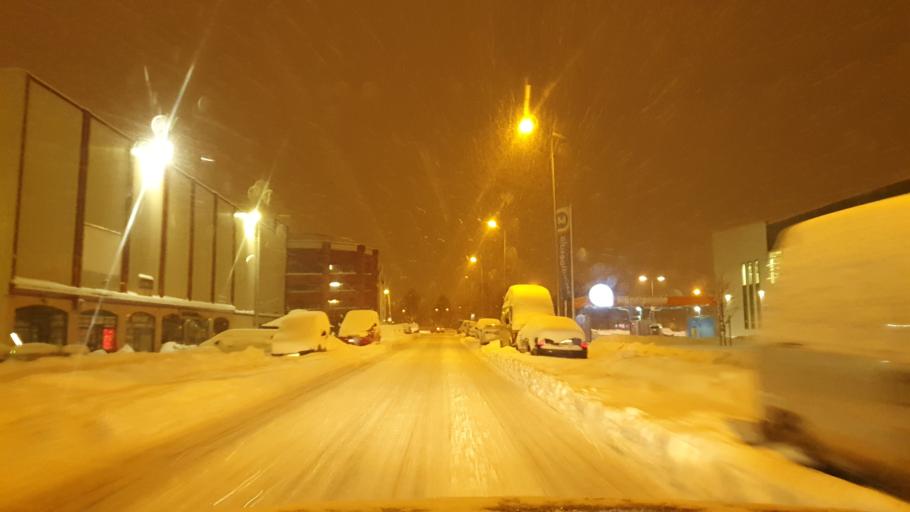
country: EE
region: Harju
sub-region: Tallinna linn
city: Kose
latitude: 59.4446
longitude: 24.8822
